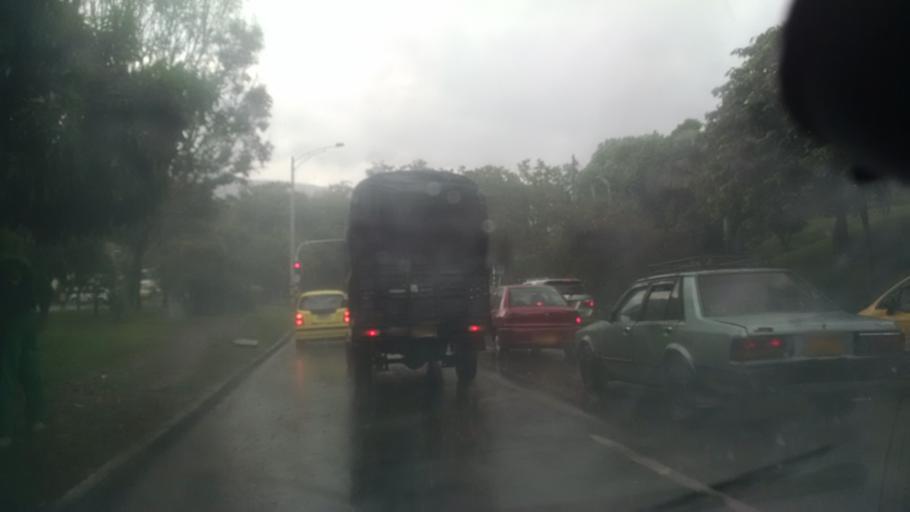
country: CO
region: Antioquia
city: Medellin
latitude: 6.2589
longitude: -75.5808
